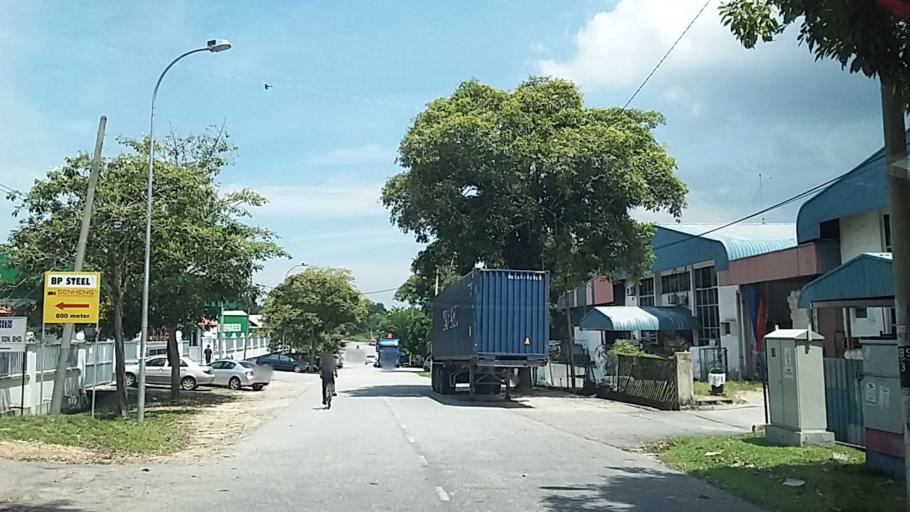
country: MY
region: Johor
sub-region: Daerah Batu Pahat
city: Batu Pahat
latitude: 1.7840
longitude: 102.9679
